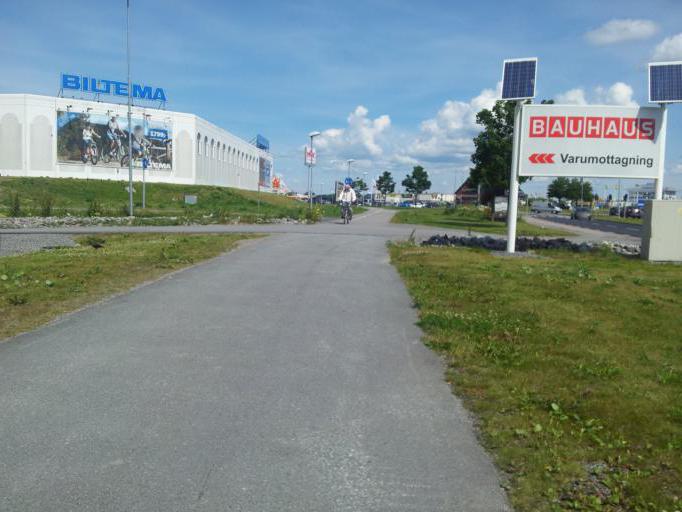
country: SE
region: Uppsala
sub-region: Uppsala Kommun
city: Saevja
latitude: 59.8488
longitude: 17.6905
